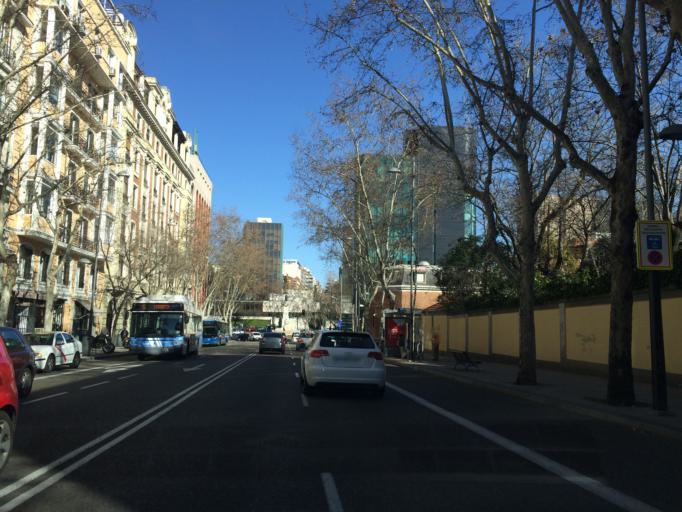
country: ES
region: Madrid
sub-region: Provincia de Madrid
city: Salamanca
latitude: 40.4351
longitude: -3.6910
